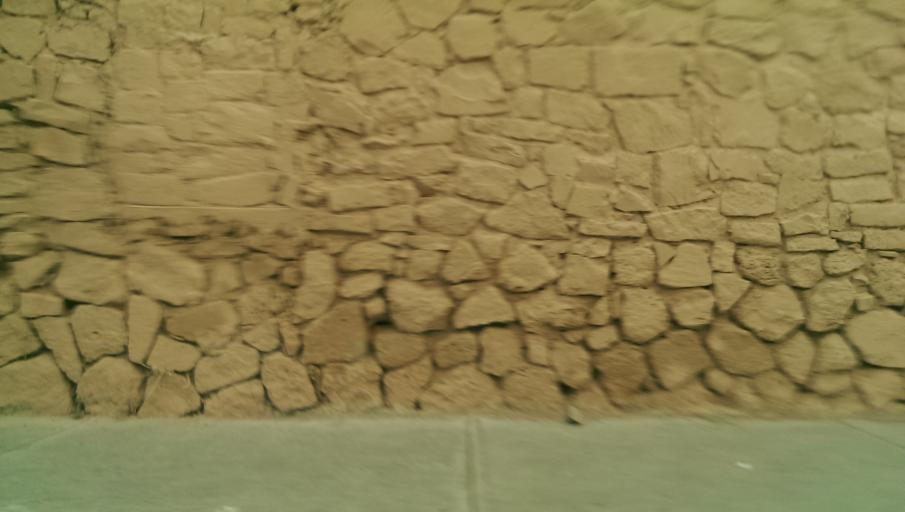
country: MX
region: Queretaro
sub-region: Queretaro
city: Santiago de Queretaro
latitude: 20.5988
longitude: -100.3700
